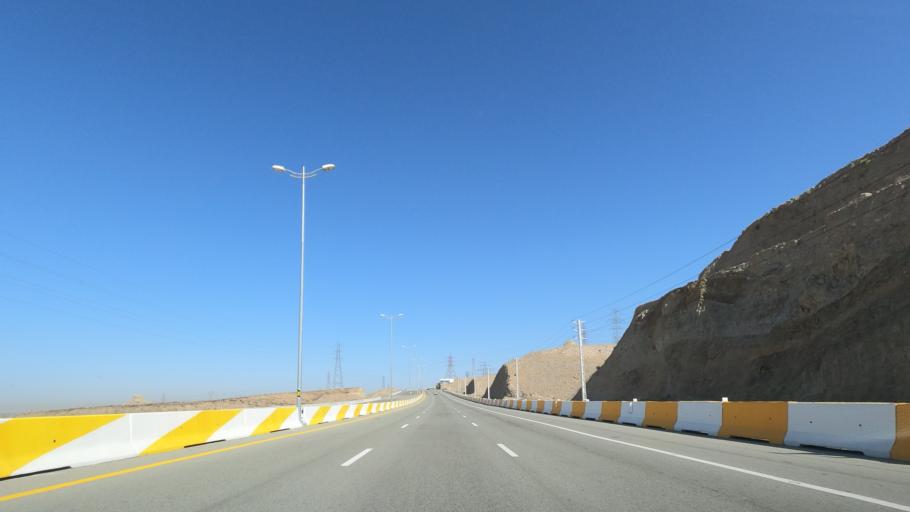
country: IR
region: Tehran
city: Shahr-e Qods
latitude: 35.7715
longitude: 51.0588
